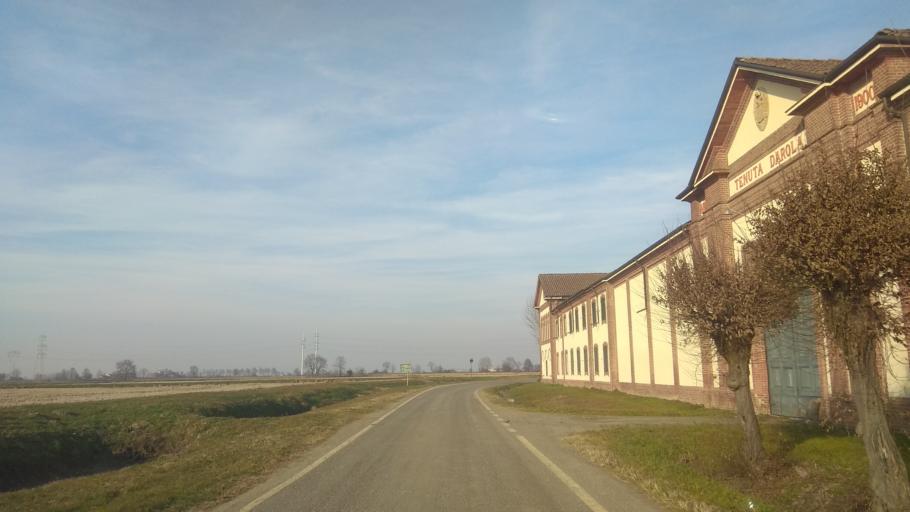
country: IT
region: Piedmont
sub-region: Provincia di Vercelli
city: Ronsecco
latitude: 45.2505
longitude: 8.2361
